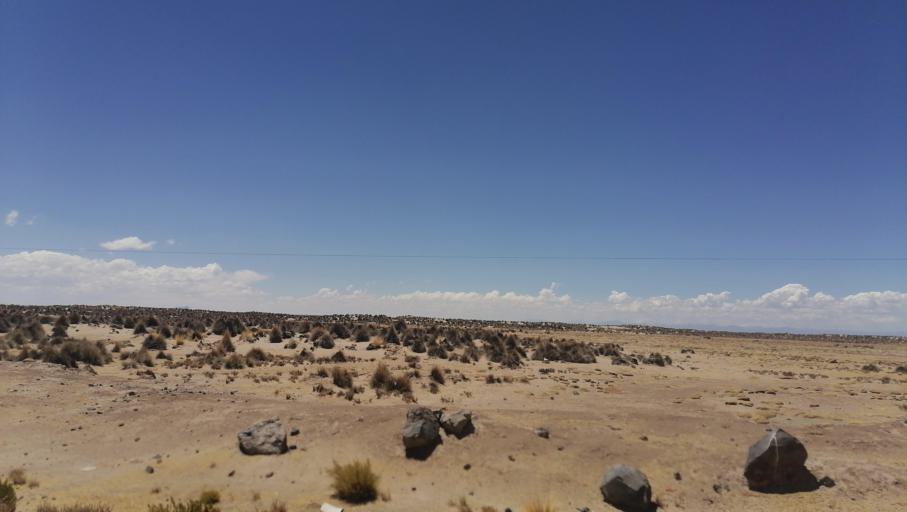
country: BO
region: Oruro
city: Challapata
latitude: -19.2220
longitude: -66.9798
